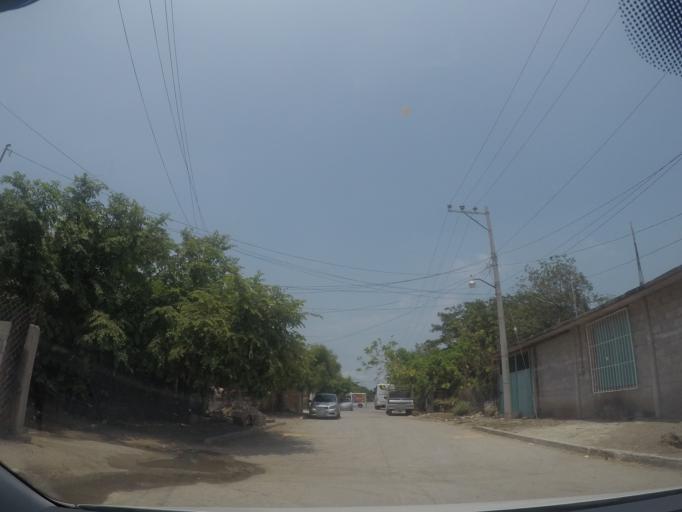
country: MX
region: Oaxaca
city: Asuncion Ixtaltepec
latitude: 16.5078
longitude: -95.0655
